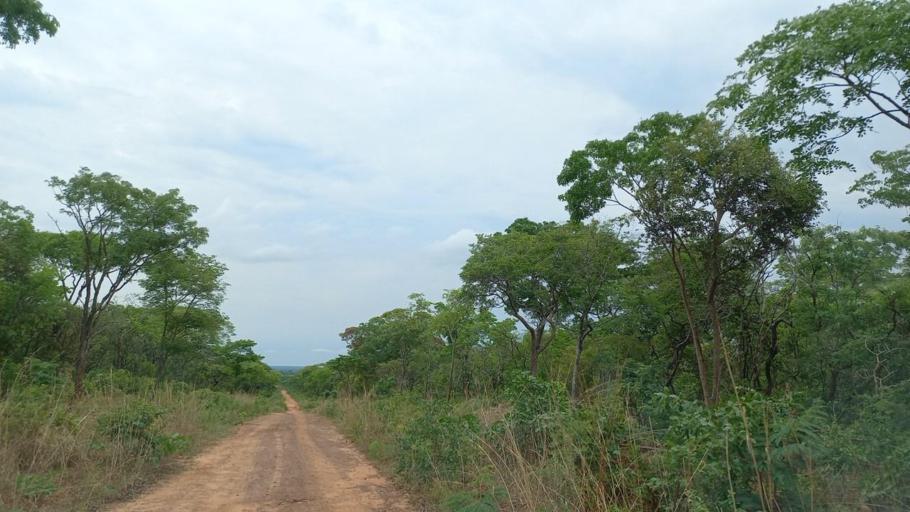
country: ZM
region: North-Western
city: Kalengwa
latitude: -13.6191
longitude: 24.9764
